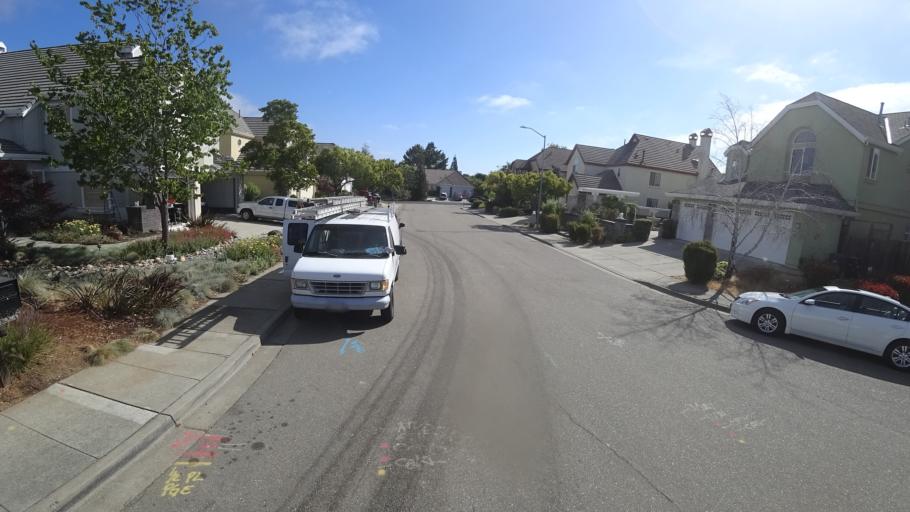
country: US
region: California
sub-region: Alameda County
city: Fairview
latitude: 37.6565
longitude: -122.0213
